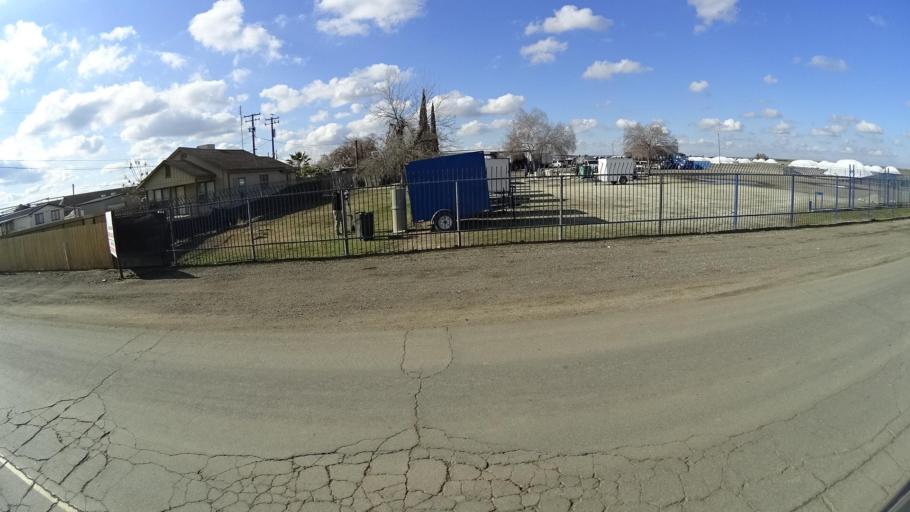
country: US
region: California
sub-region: Kern County
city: McFarland
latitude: 35.6963
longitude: -119.2408
